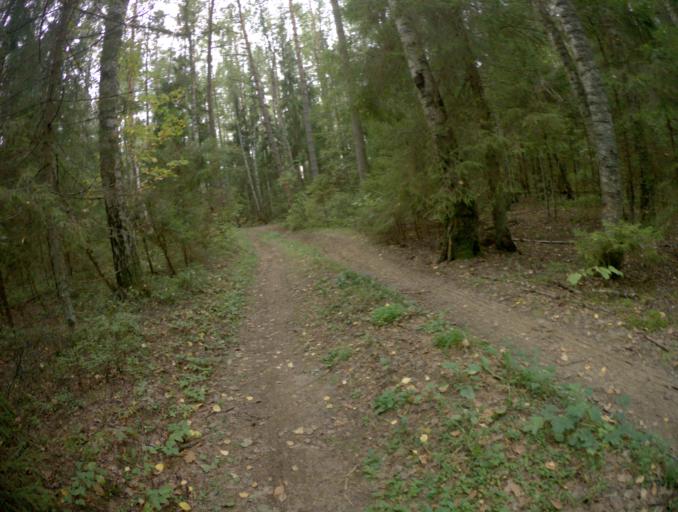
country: RU
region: Vladimir
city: Golovino
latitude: 55.9895
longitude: 40.4643
